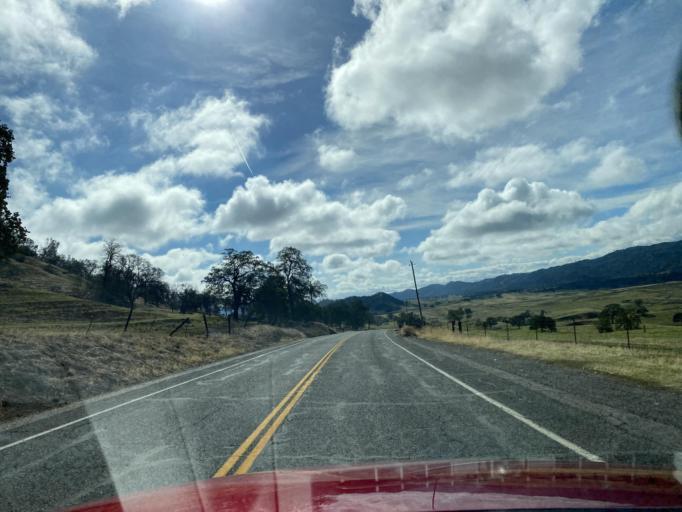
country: US
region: California
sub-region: Glenn County
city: Willows
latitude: 39.5522
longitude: -122.5399
